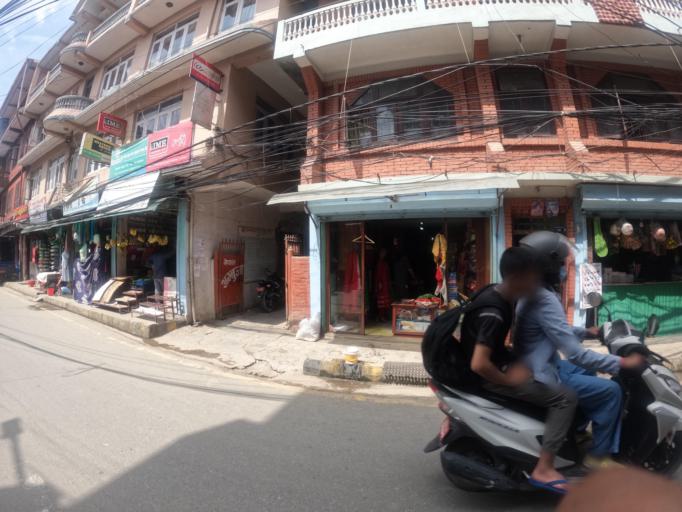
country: NP
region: Central Region
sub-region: Bagmati Zone
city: Patan
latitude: 27.6770
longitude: 85.3617
